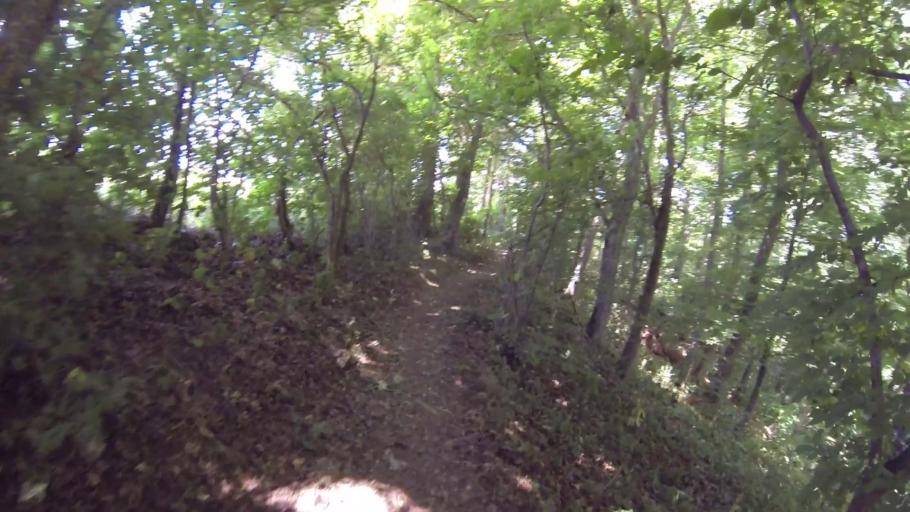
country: DE
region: Baden-Wuerttemberg
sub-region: Regierungsbezirk Stuttgart
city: Herbrechtingen
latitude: 48.6056
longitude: 10.1571
